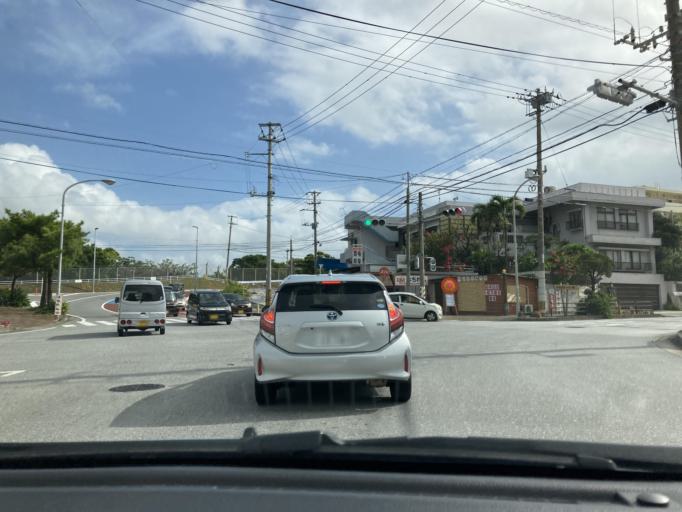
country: JP
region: Okinawa
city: Ginowan
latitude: 26.2633
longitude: 127.7484
